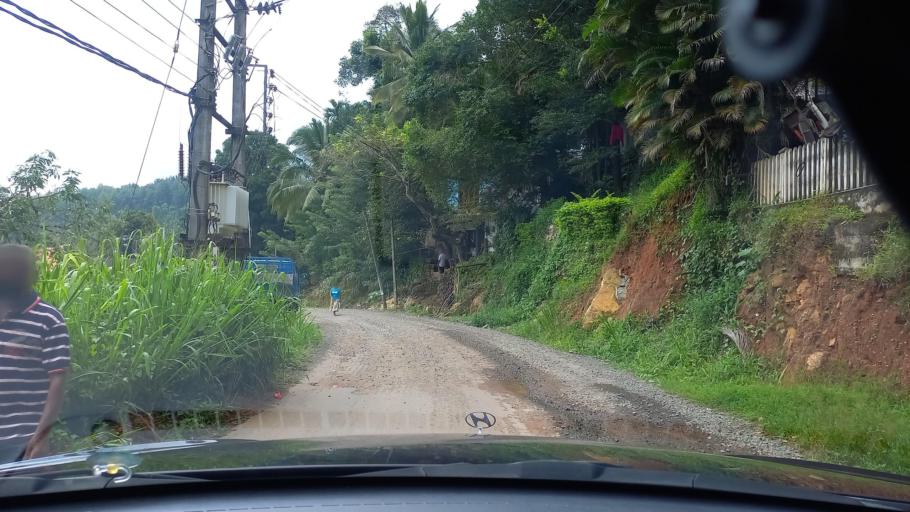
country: LK
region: Central
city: Gampola
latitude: 7.2142
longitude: 80.6144
